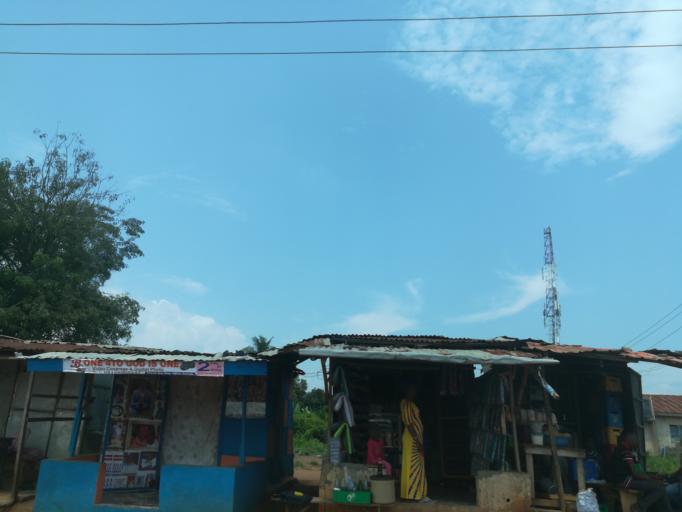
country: NG
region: Lagos
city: Ikorodu
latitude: 6.5790
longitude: 3.6276
